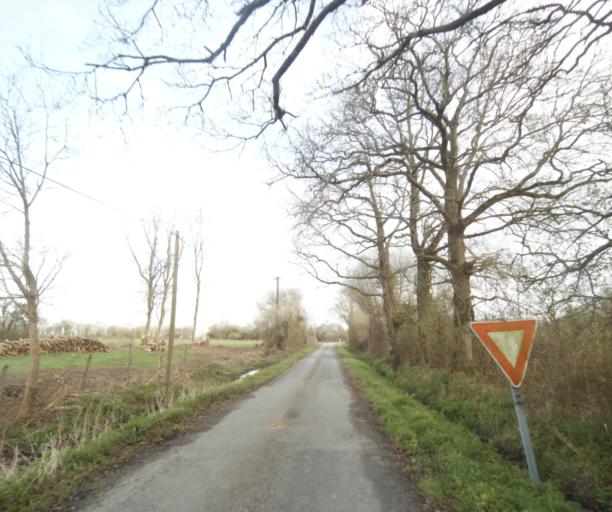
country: FR
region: Pays de la Loire
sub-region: Departement de la Loire-Atlantique
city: Bouvron
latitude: 47.4168
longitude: -1.8751
